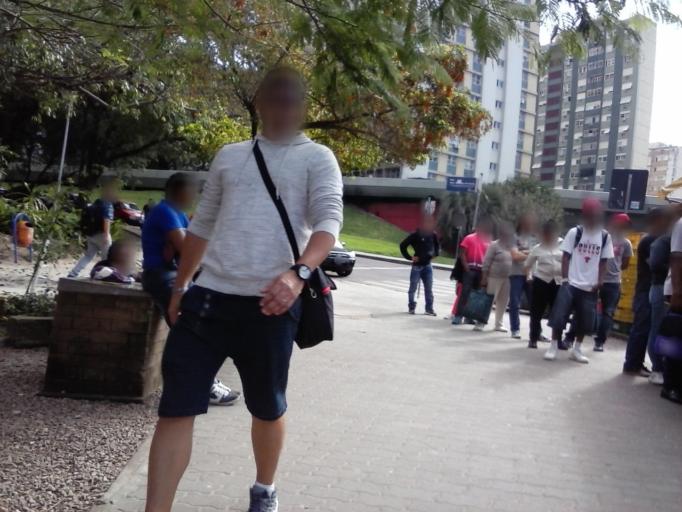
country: BR
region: Rio Grande do Sul
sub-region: Porto Alegre
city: Porto Alegre
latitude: -30.0320
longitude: -51.2235
